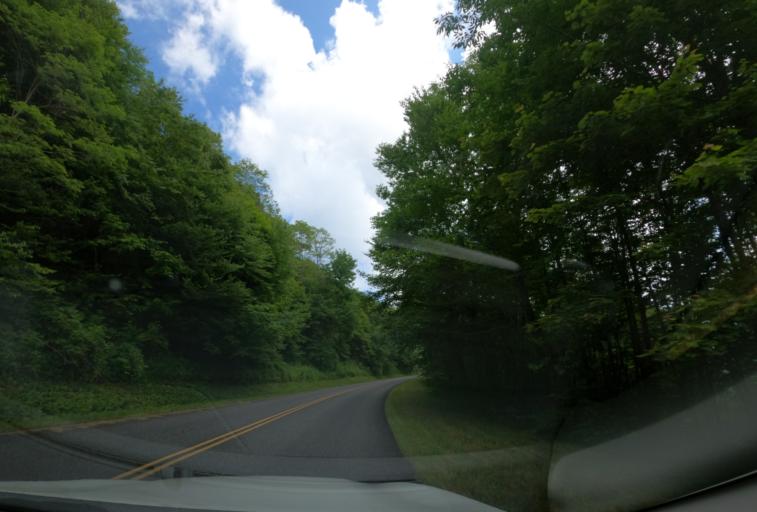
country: US
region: North Carolina
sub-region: Haywood County
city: Hazelwood
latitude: 35.4145
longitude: -83.0411
